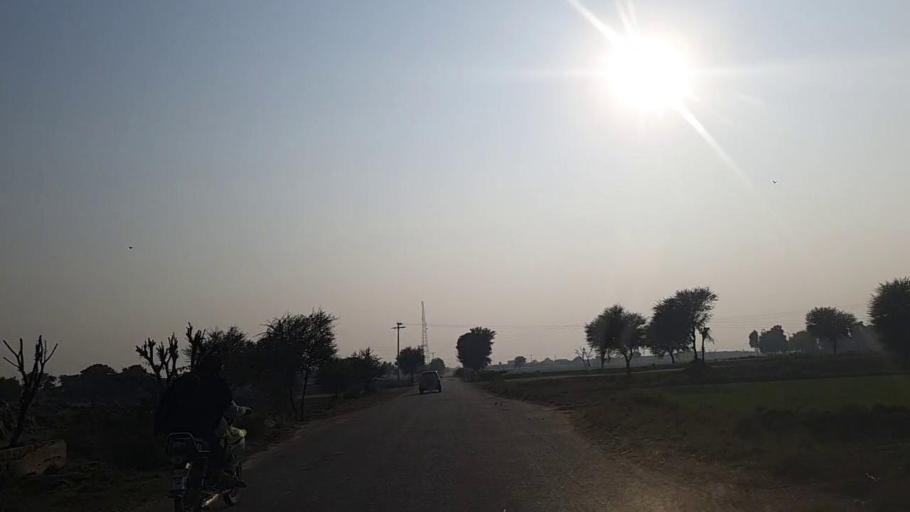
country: PK
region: Sindh
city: Shahpur Chakar
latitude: 26.2034
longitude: 68.5590
